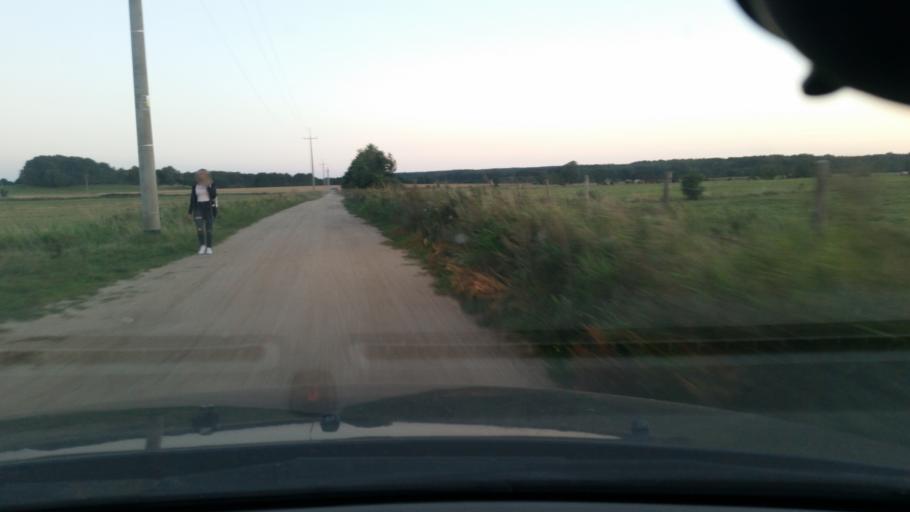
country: PL
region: Pomeranian Voivodeship
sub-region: Powiat wejherowski
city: Choczewo
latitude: 54.7785
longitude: 17.7929
